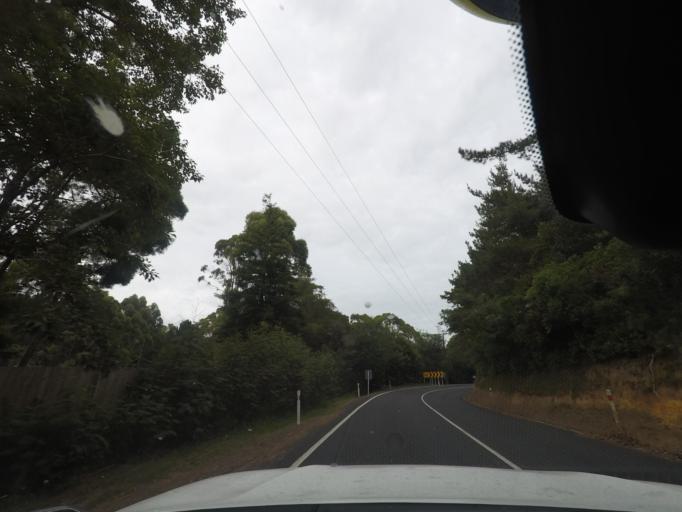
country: NZ
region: Auckland
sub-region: Auckland
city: Parakai
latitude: -36.5216
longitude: 174.2758
